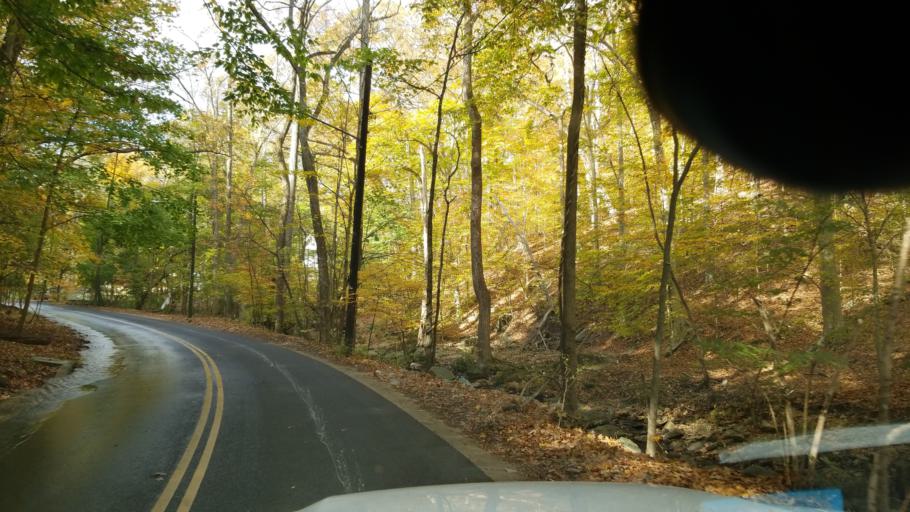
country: US
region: Maryland
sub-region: Montgomery County
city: Chevy Chase
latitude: 38.9573
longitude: -77.0587
